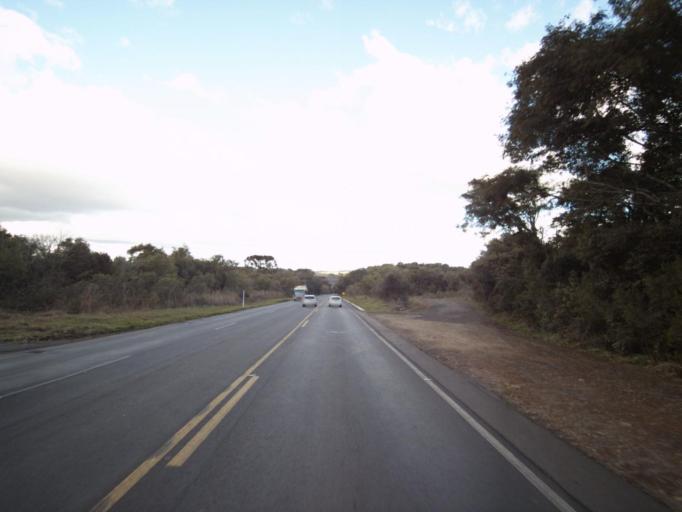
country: BR
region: Santa Catarina
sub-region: Campos Novos
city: Campos Novos
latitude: -27.3074
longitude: -51.3775
